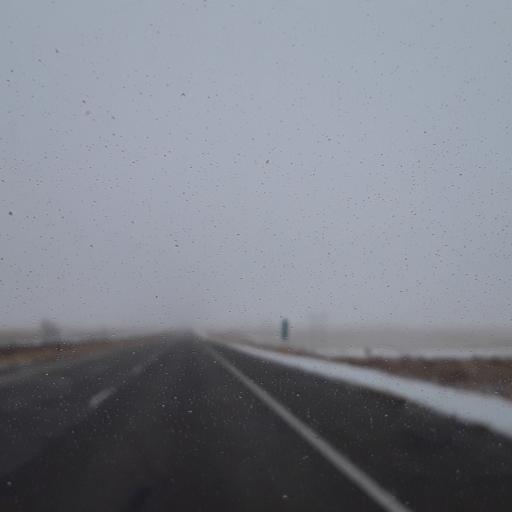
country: US
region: Colorado
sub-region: Logan County
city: Sterling
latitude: 40.7915
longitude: -102.8885
